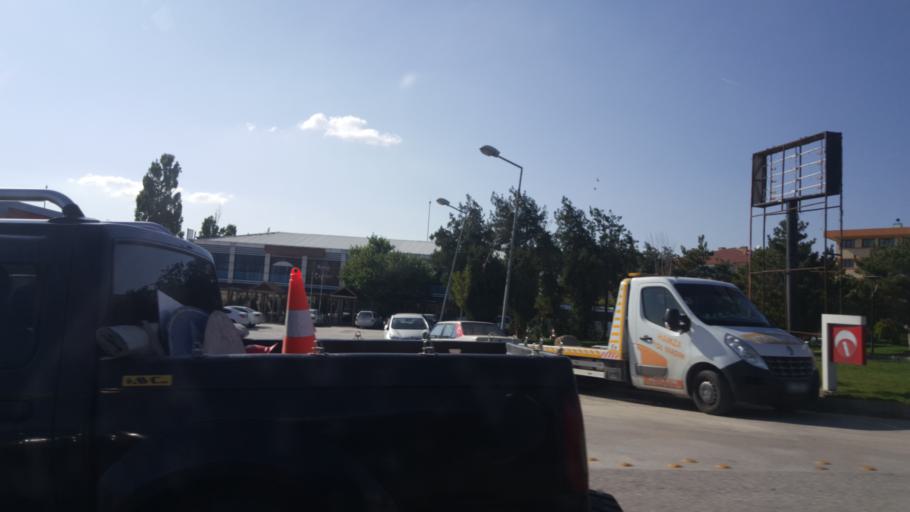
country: TR
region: Ankara
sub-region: Goelbasi
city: Golbasi
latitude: 39.8053
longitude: 32.8042
